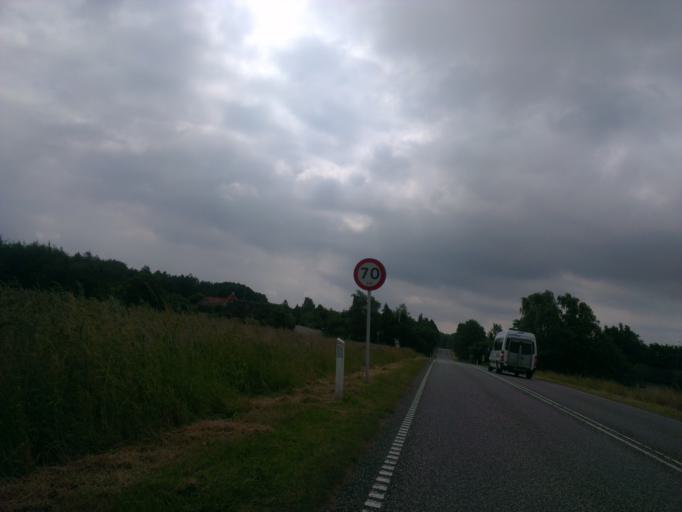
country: DK
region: Capital Region
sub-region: Frederikssund Kommune
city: Jaegerspris
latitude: 55.9098
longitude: 11.9348
